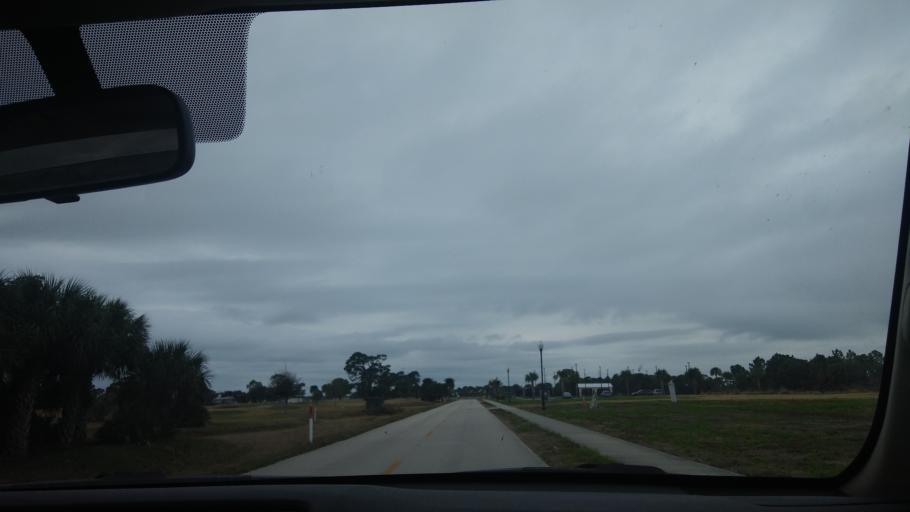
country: US
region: Florida
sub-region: Indian River County
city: Sebastian
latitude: 27.8110
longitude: -80.4871
